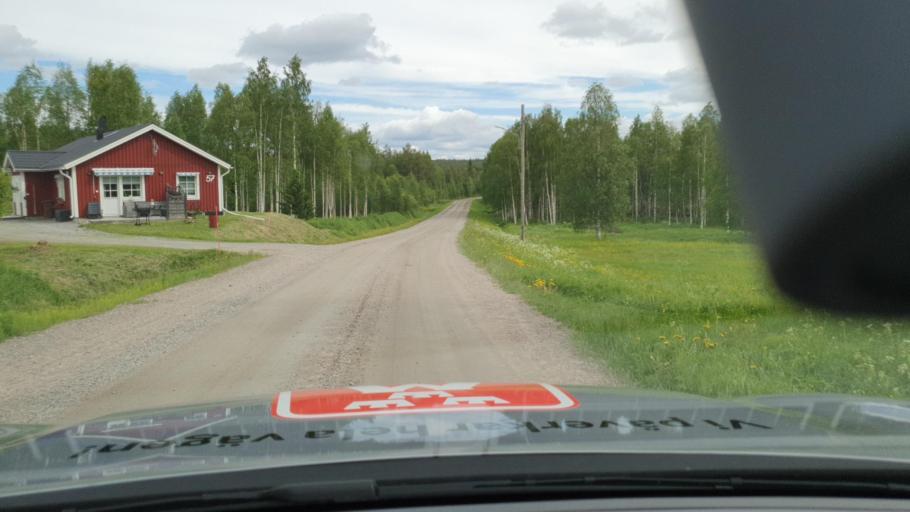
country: SE
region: Norrbotten
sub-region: Kalix Kommun
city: Kalix
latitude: 65.9392
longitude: 23.5290
